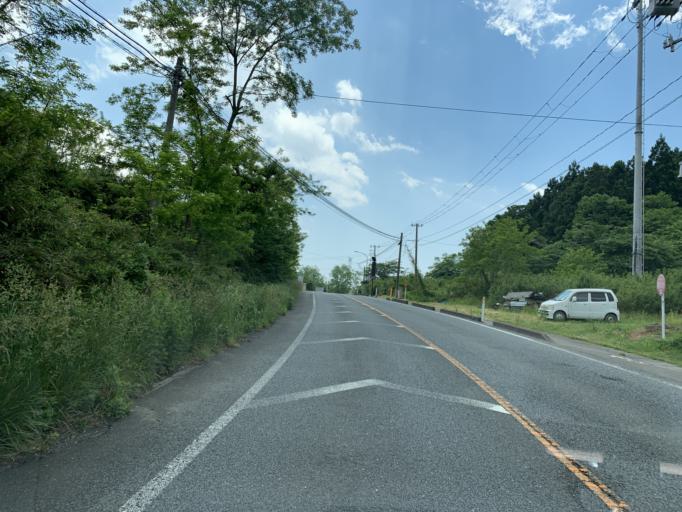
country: JP
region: Miyagi
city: Matsushima
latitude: 38.4186
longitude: 141.0597
